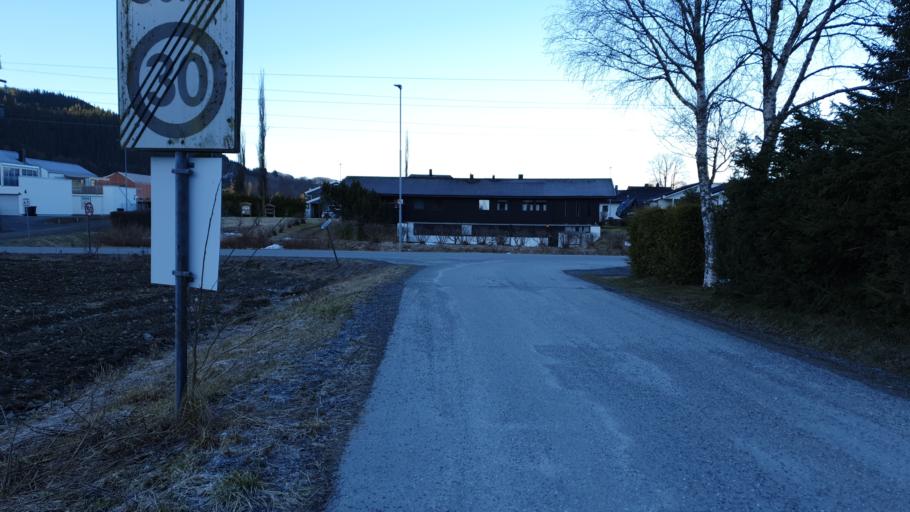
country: NO
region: Sor-Trondelag
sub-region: Orkdal
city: Orkanger
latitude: 63.2897
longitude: 9.8463
